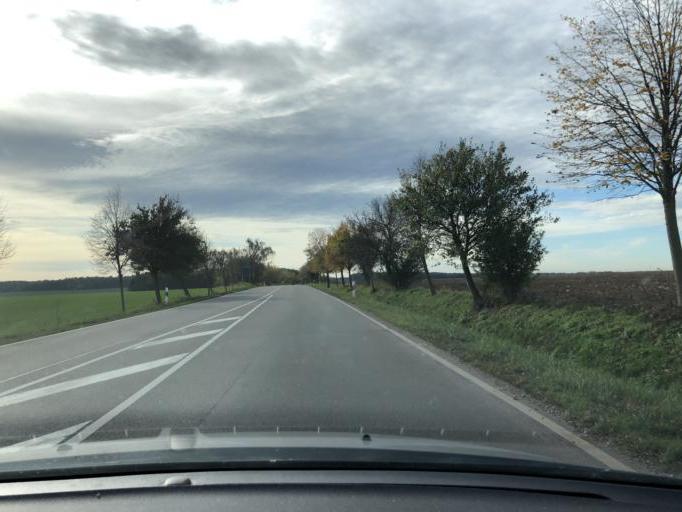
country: DE
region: Thuringia
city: Hirschfeld
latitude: 50.9811
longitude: 12.1358
